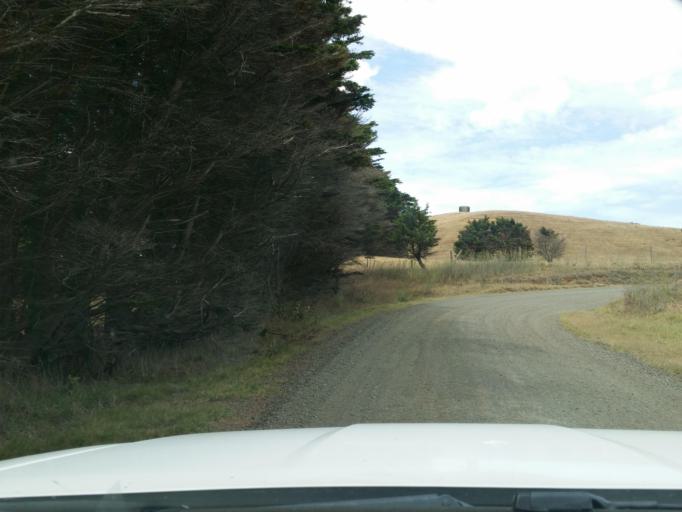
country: NZ
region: Auckland
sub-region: Auckland
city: Wellsford
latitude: -36.3438
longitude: 174.1681
